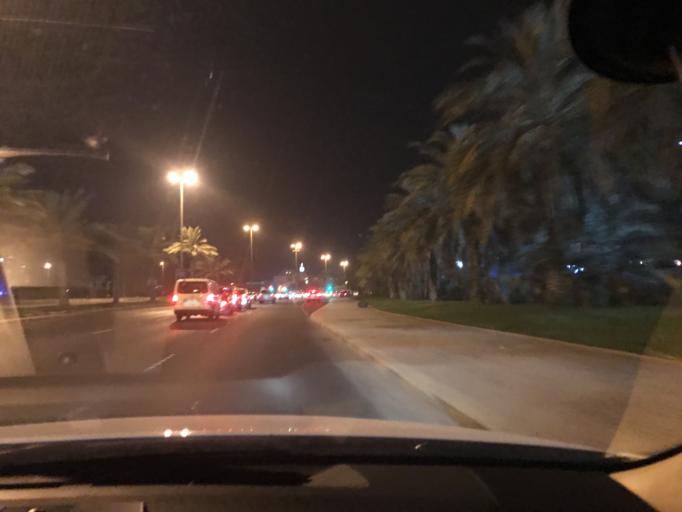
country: BH
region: Muharraq
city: Al Muharraq
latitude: 26.2438
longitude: 50.6114
